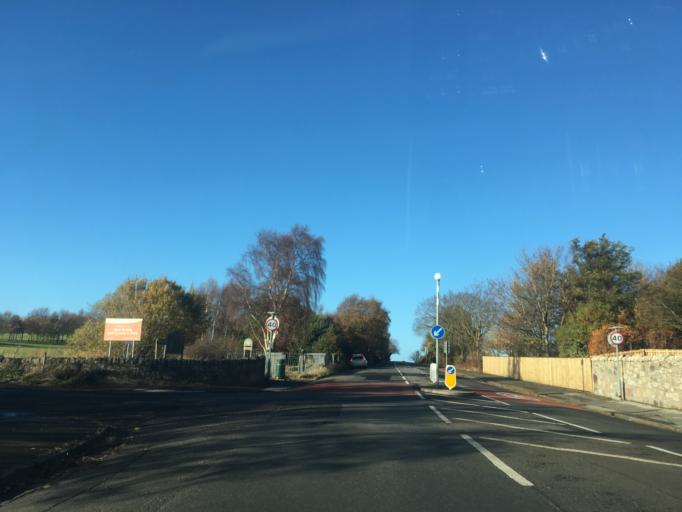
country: GB
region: Scotland
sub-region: Midlothian
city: Loanhead
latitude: 55.9136
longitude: -3.1779
